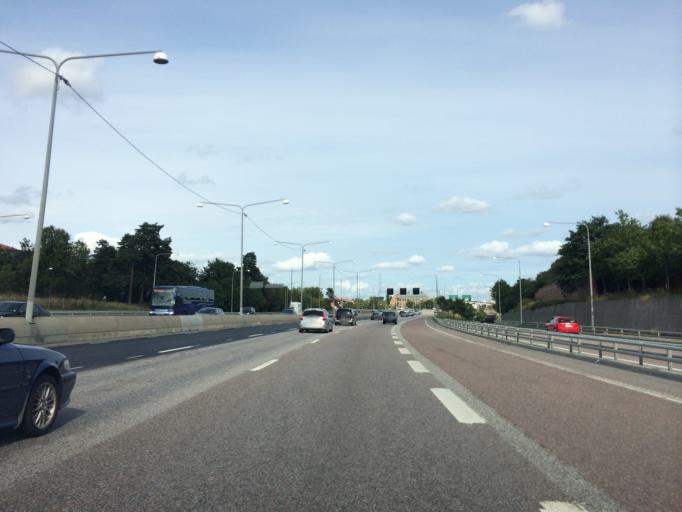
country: SE
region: Stockholm
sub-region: Stockholms Kommun
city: Arsta
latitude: 59.2982
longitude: 18.0077
